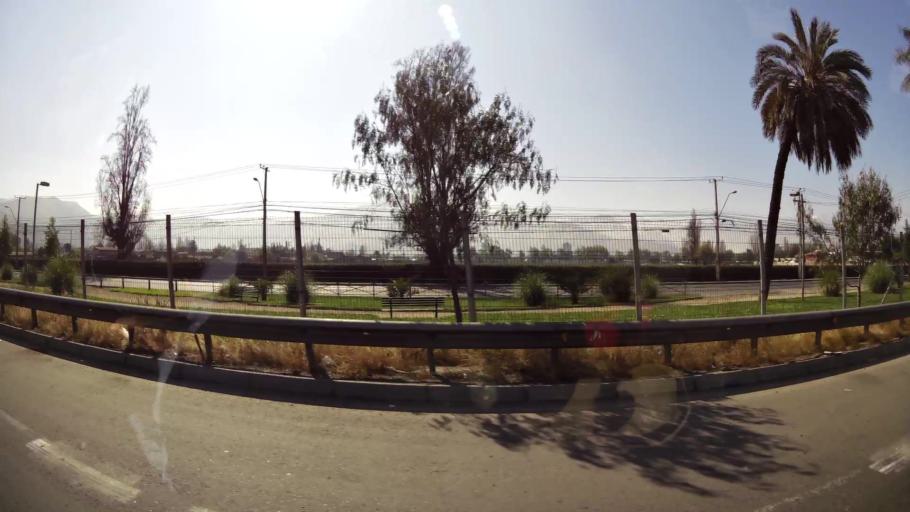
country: CL
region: Santiago Metropolitan
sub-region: Provincia de Chacabuco
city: Chicureo Abajo
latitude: -33.3623
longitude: -70.6898
